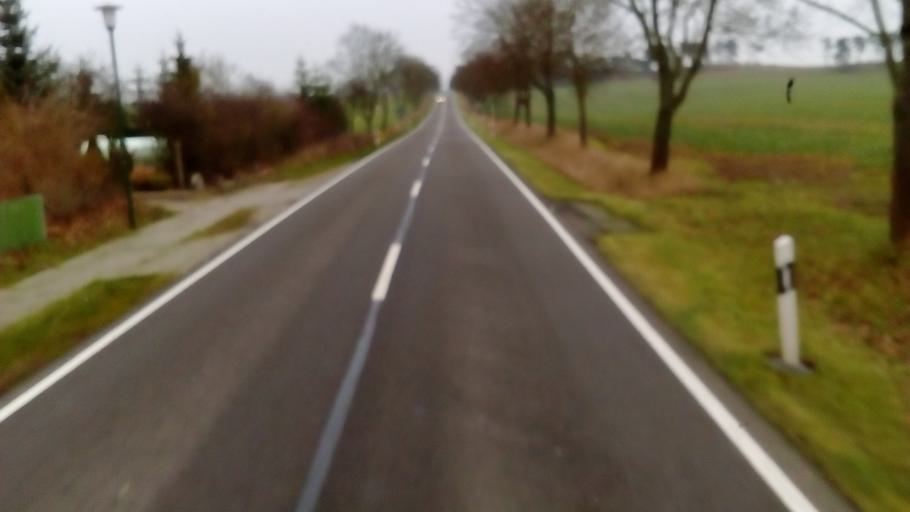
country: DE
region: Brandenburg
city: Goritz
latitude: 53.4924
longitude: 13.8829
